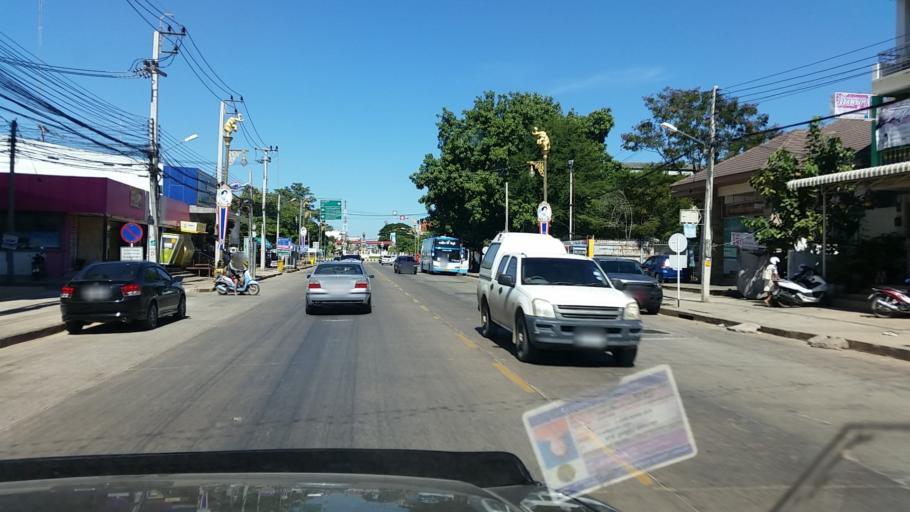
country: TH
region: Chaiyaphum
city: Chaiyaphum
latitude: 15.8047
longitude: 102.0313
